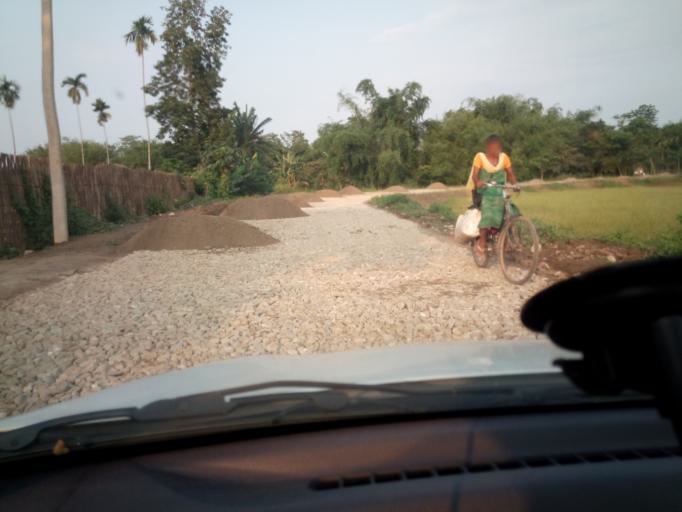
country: IN
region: Assam
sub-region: Udalguri
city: Udalguri
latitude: 26.7028
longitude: 92.0883
